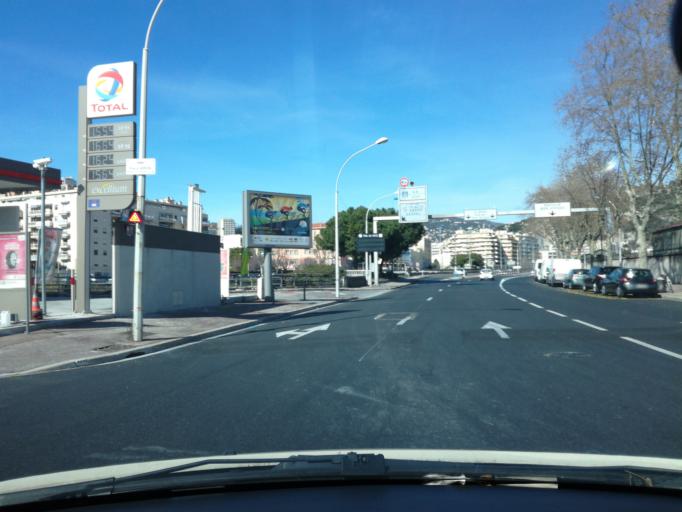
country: FR
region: Provence-Alpes-Cote d'Azur
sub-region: Departement des Alpes-Maritimes
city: Saint-Andre-de-la-Roche
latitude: 43.7164
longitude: 7.2826
